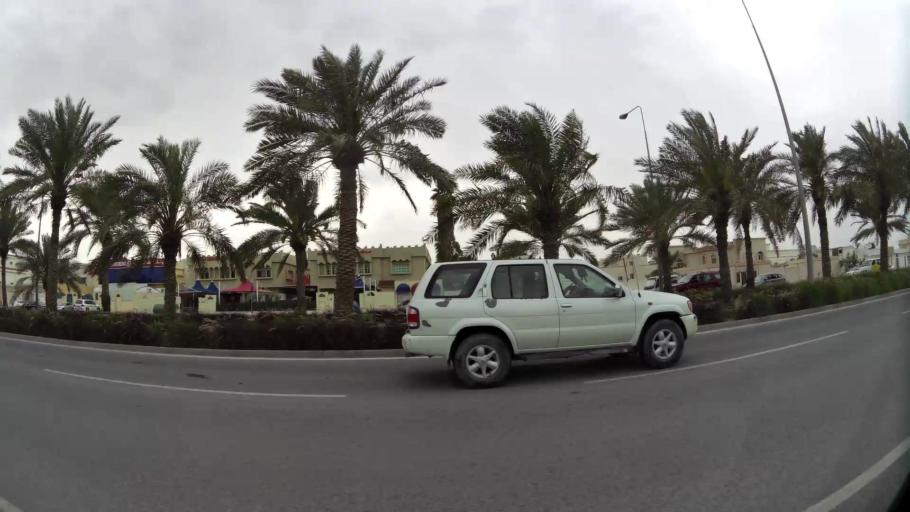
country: QA
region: Baladiyat ad Dawhah
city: Doha
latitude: 25.3089
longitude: 51.4877
